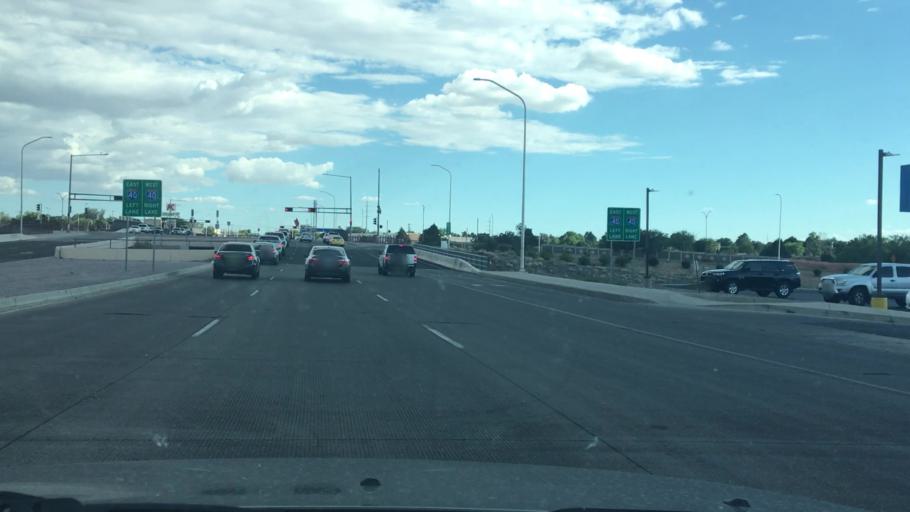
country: US
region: New Mexico
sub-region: Bernalillo County
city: Albuquerque
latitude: 35.1071
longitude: -106.6043
